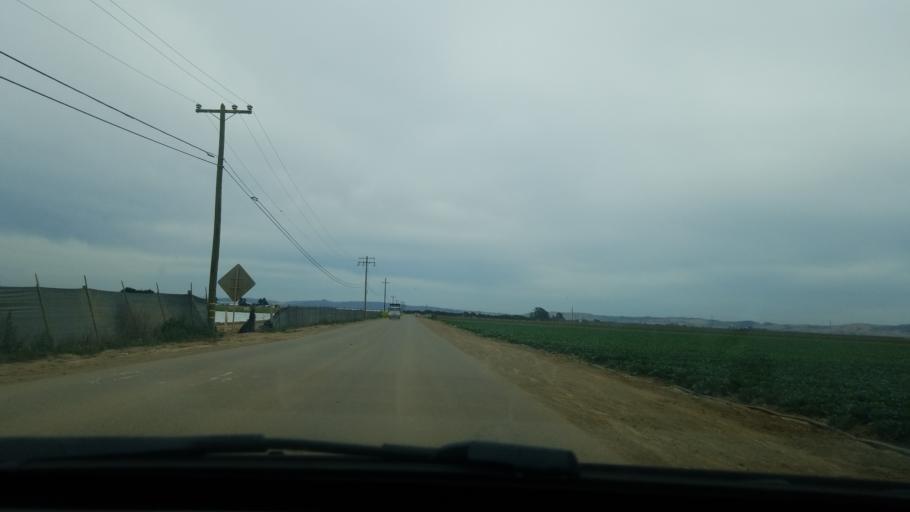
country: US
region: California
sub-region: San Luis Obispo County
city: Nipomo
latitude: 35.0028
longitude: -120.5186
